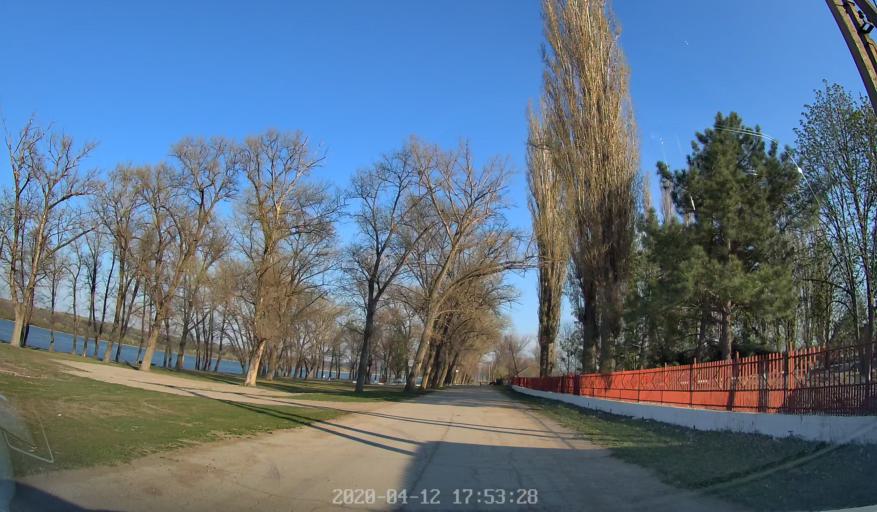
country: MD
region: Telenesti
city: Cocieri
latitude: 47.3833
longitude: 29.1236
